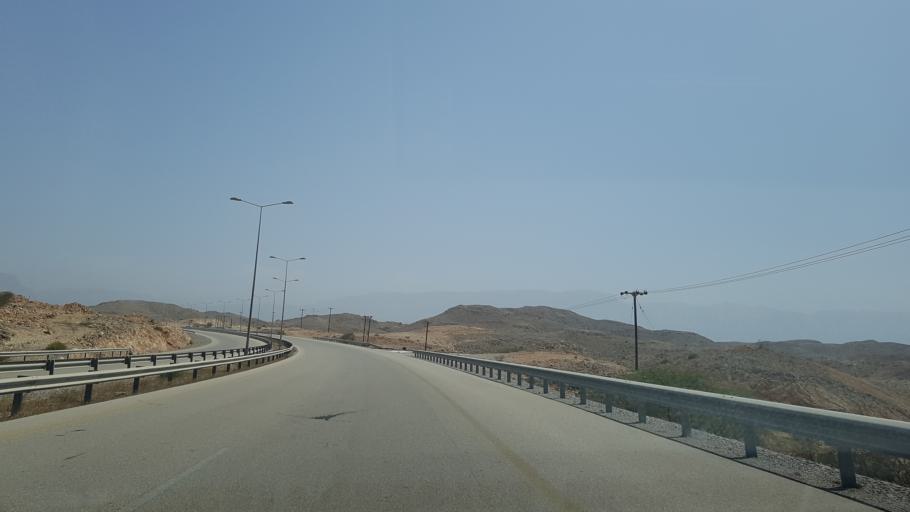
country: OM
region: Muhafazat Masqat
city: Muscat
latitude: 23.1651
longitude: 58.9749
